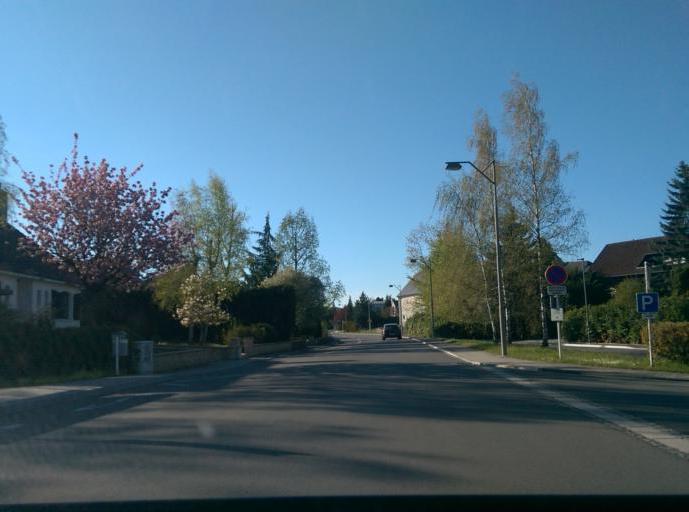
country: LU
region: Luxembourg
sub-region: Canton de Luxembourg
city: Niederanven
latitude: 49.6515
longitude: 6.2549
